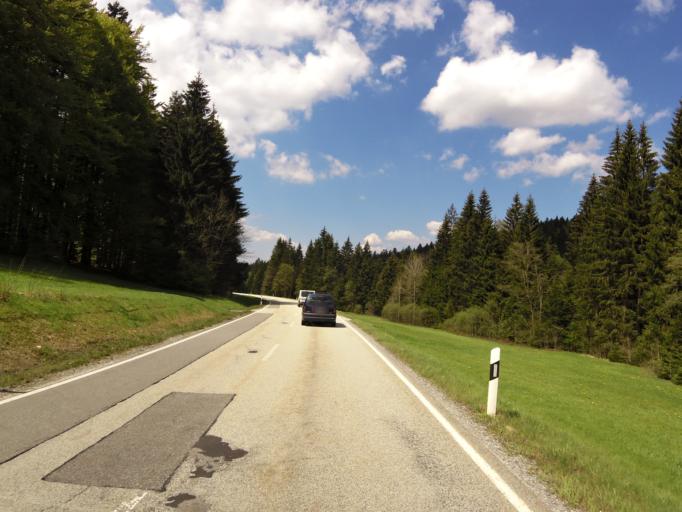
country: DE
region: Bavaria
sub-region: Lower Bavaria
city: Hinterschmiding
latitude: 48.8451
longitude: 13.6273
